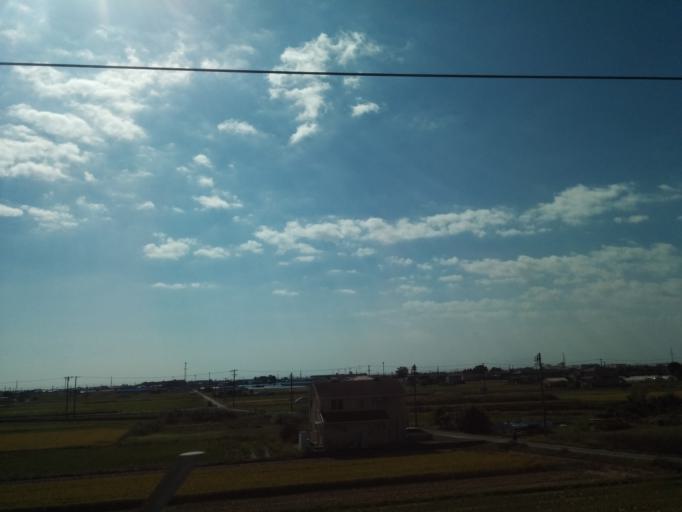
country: JP
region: Shizuoka
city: Iwata
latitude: 34.7029
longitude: 137.8137
